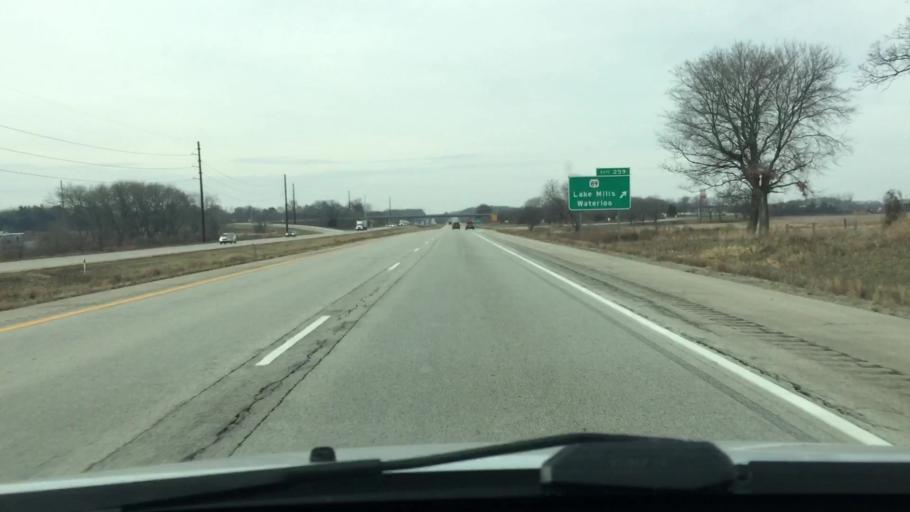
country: US
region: Wisconsin
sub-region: Jefferson County
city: Lake Mills
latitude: 43.0913
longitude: -88.9021
